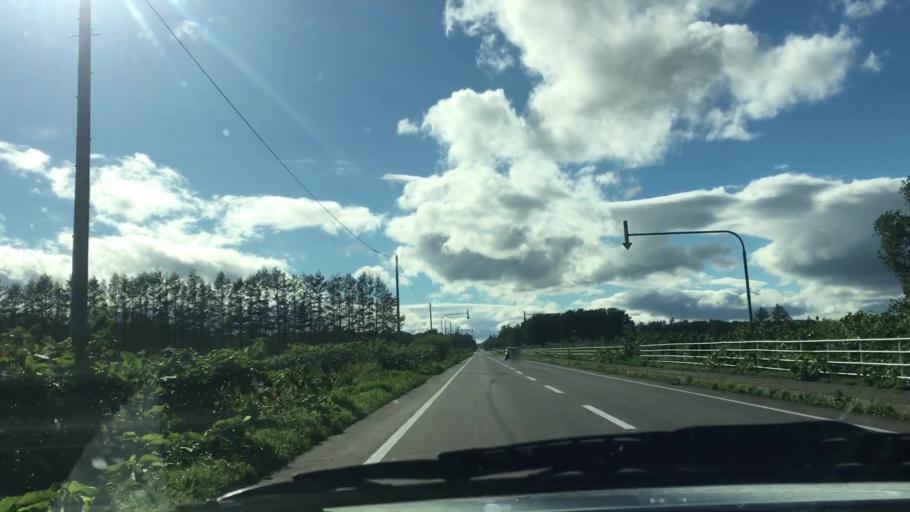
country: JP
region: Hokkaido
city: Otofuke
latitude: 43.1672
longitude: 143.1279
